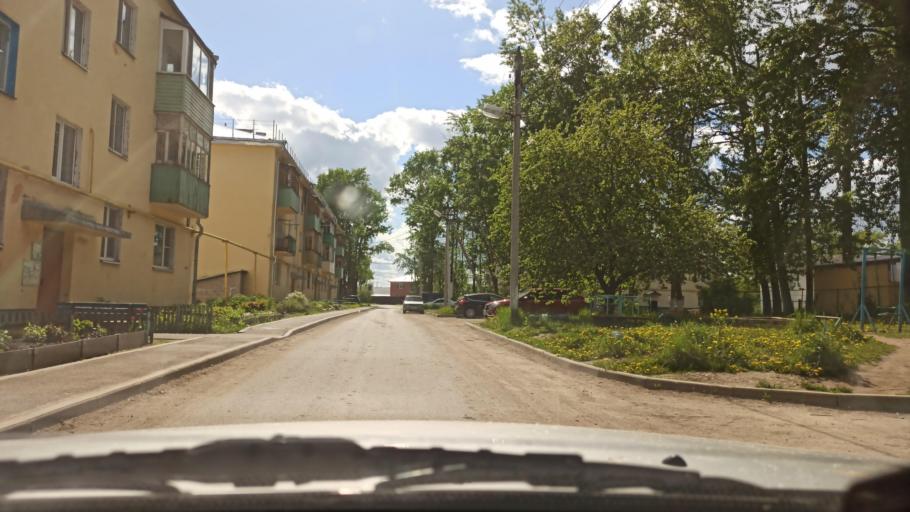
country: RU
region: Vologda
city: Vologda
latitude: 59.3417
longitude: 39.8132
